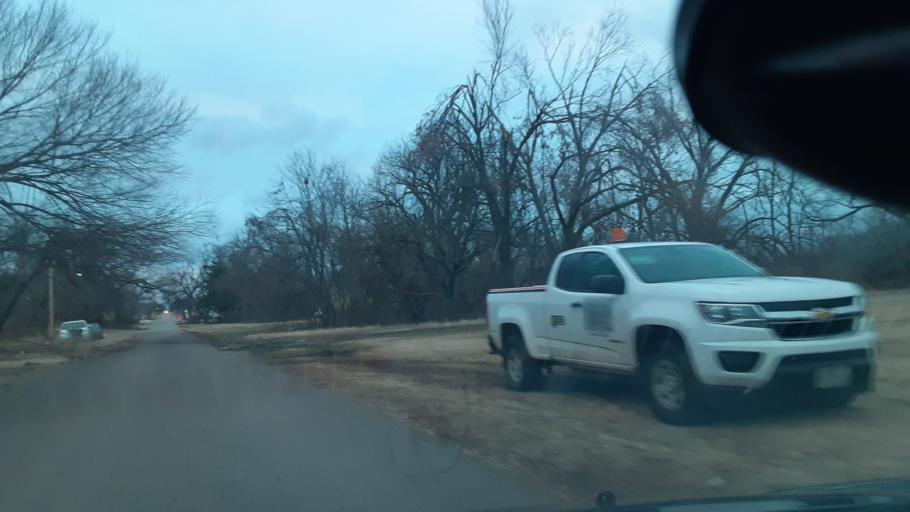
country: US
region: Oklahoma
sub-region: Logan County
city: Guthrie
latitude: 35.8738
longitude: -97.4299
